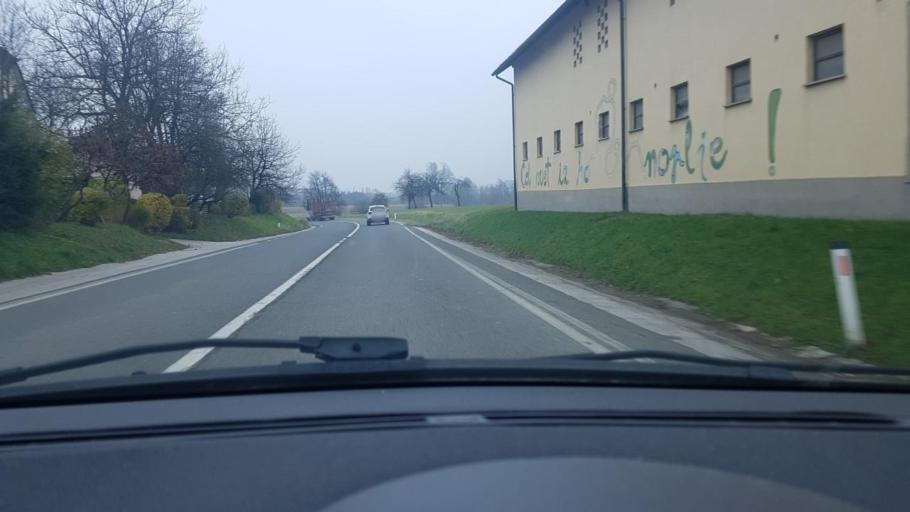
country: SI
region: Tabor
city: Tabor
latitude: 46.2474
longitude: 15.0101
